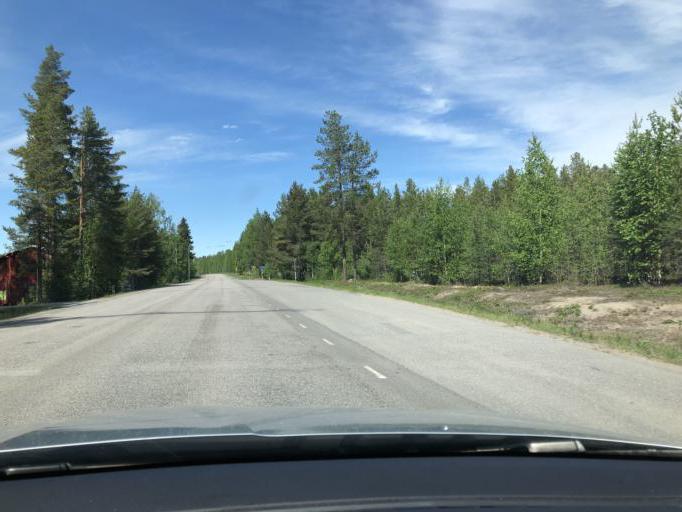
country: SE
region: Norrbotten
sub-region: Pitea Kommun
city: Bergsviken
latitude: 65.3797
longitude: 21.3413
